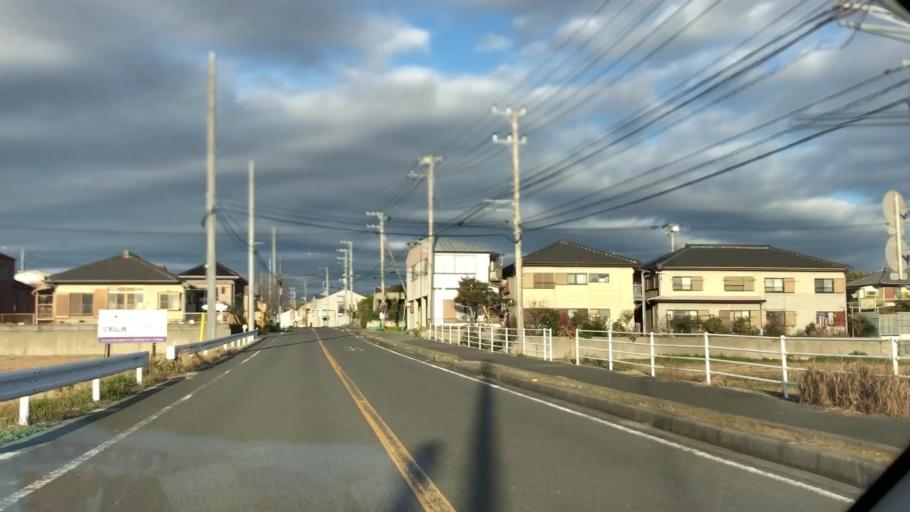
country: JP
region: Chiba
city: Tateyama
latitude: 34.9745
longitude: 139.9599
